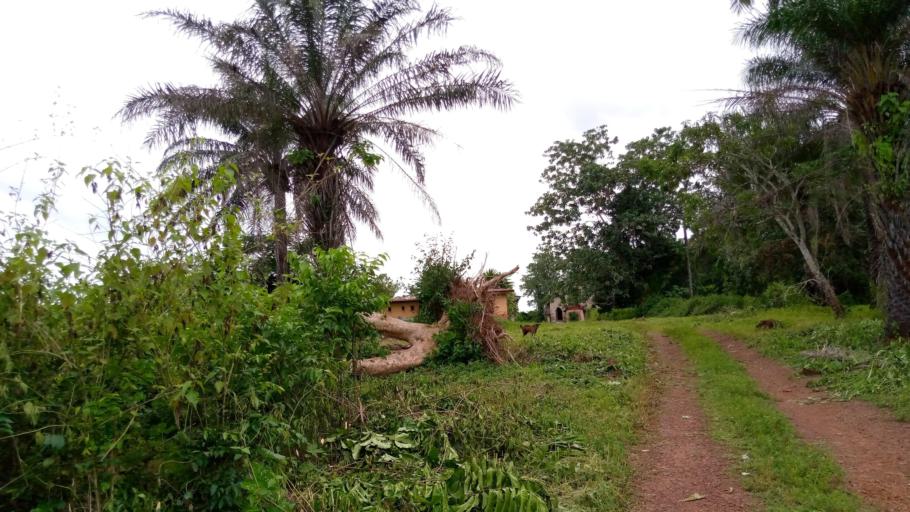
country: SL
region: Southern Province
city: Rotifunk
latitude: 8.1910
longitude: -12.5650
